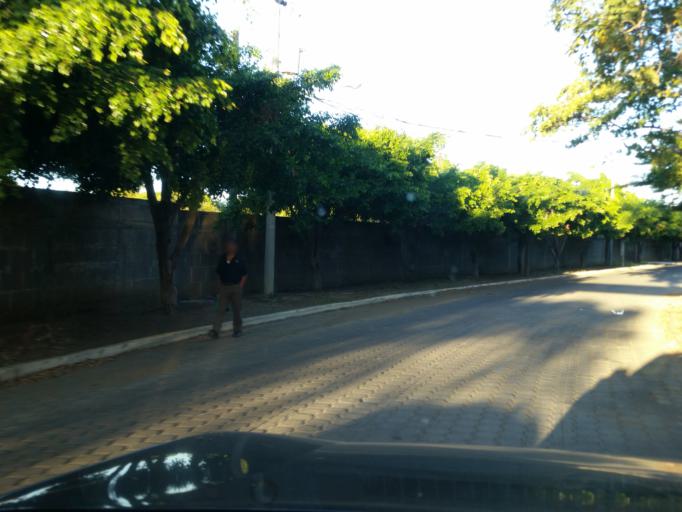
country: NI
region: Managua
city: Managua
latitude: 12.0898
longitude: -86.2329
